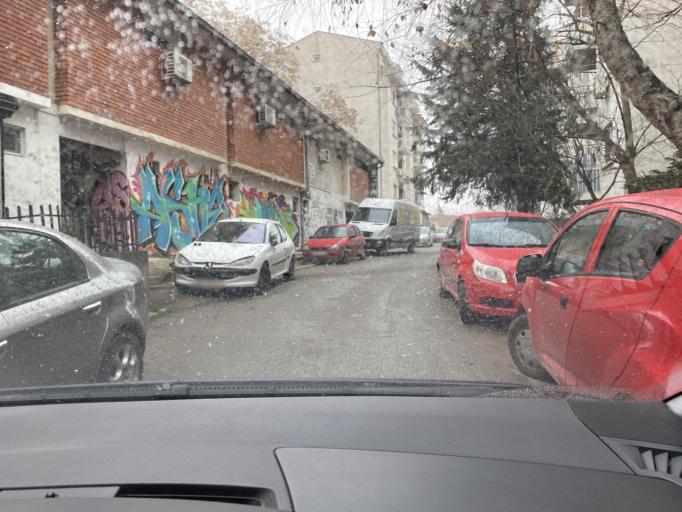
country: MK
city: Radishani
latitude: 42.0598
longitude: 21.4502
